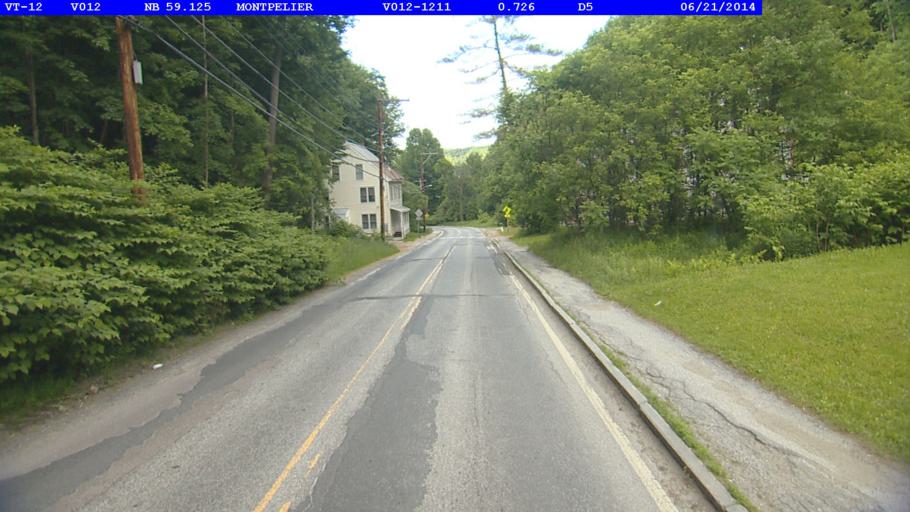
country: US
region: Vermont
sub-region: Washington County
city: Montpelier
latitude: 44.2544
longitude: -72.5799
